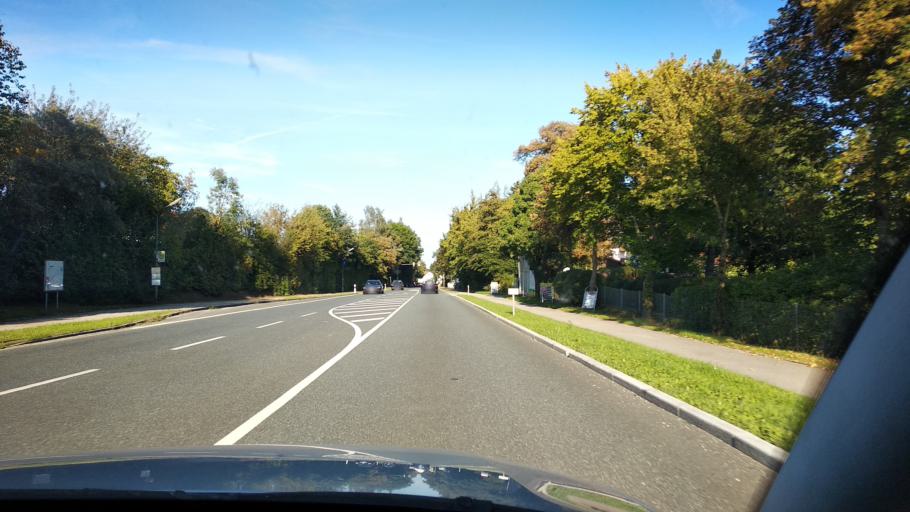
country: DE
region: Bavaria
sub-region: Upper Bavaria
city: Steinhoring
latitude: 48.0851
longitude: 12.0242
